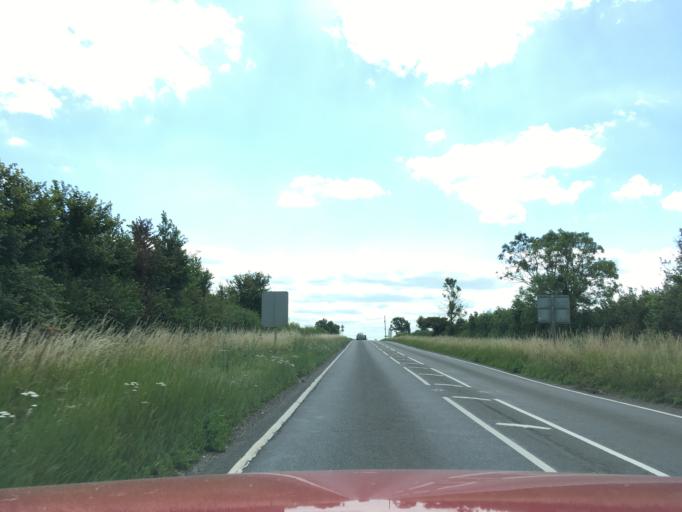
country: GB
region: England
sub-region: Buckinghamshire
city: Winslow
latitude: 51.9167
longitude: -0.8411
